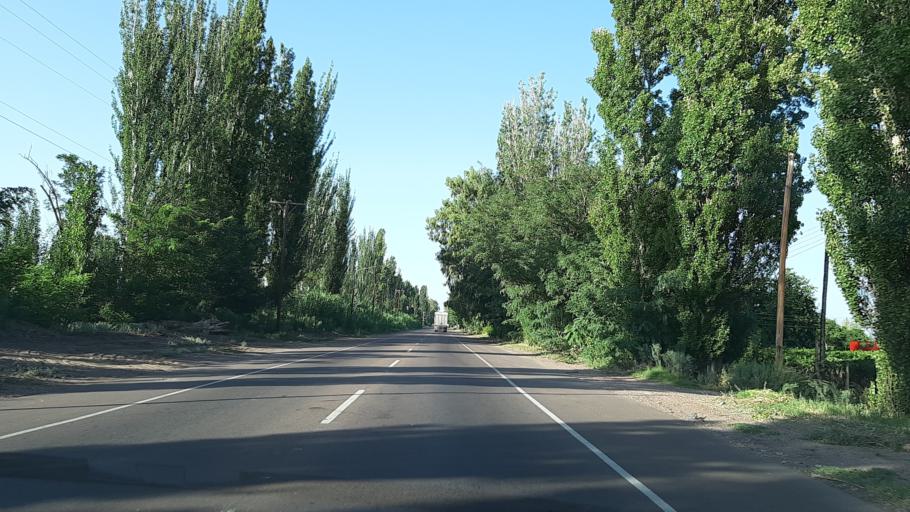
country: AR
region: Mendoza
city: San Martin
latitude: -33.0250
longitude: -68.5044
